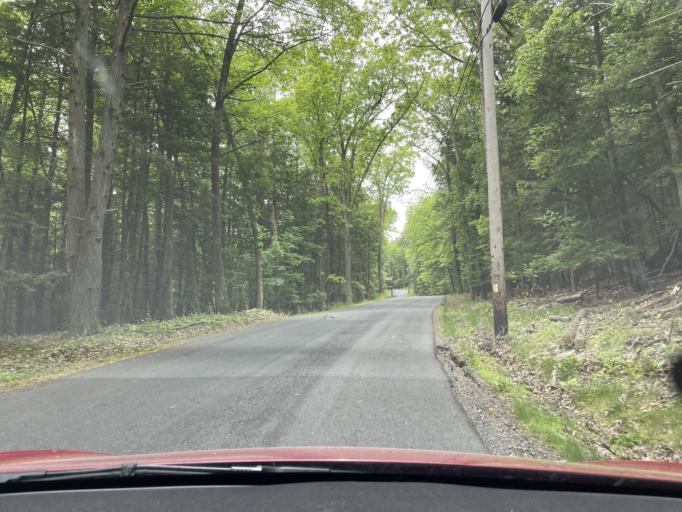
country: US
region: New York
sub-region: Ulster County
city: Zena
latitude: 41.9932
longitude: -74.0592
